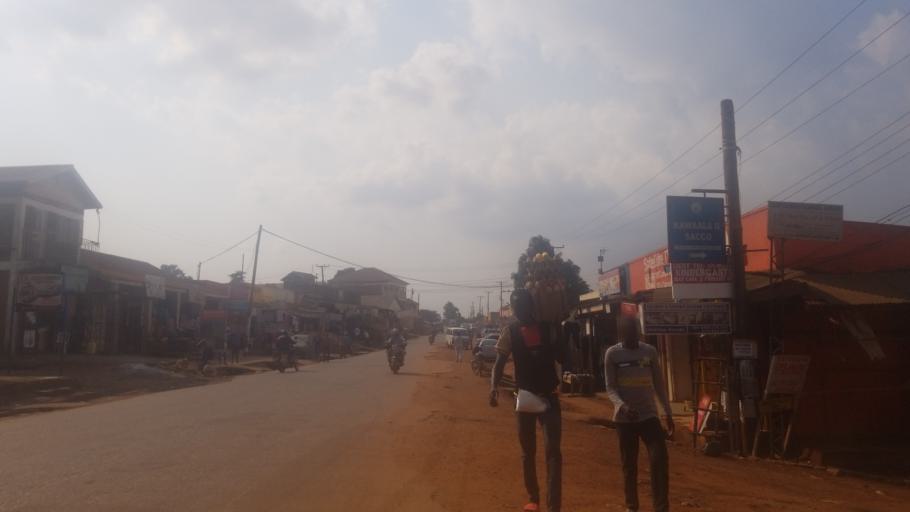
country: UG
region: Central Region
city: Kampala Central Division
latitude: 0.3344
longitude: 32.5558
